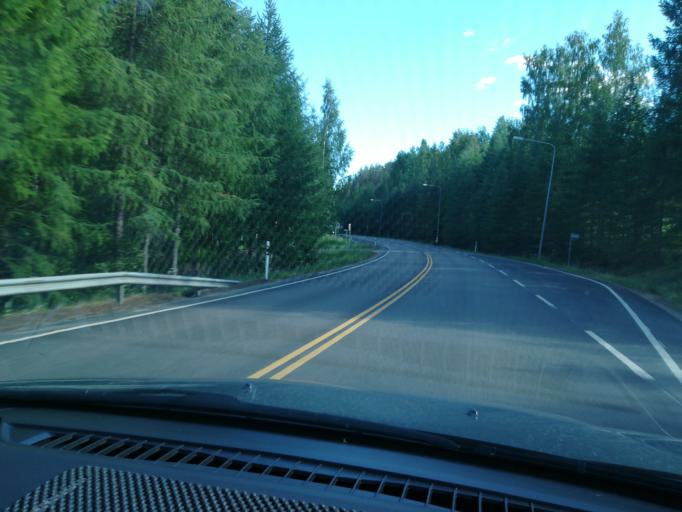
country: FI
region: Southern Savonia
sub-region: Mikkeli
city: Puumala
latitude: 61.5159
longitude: 28.1733
